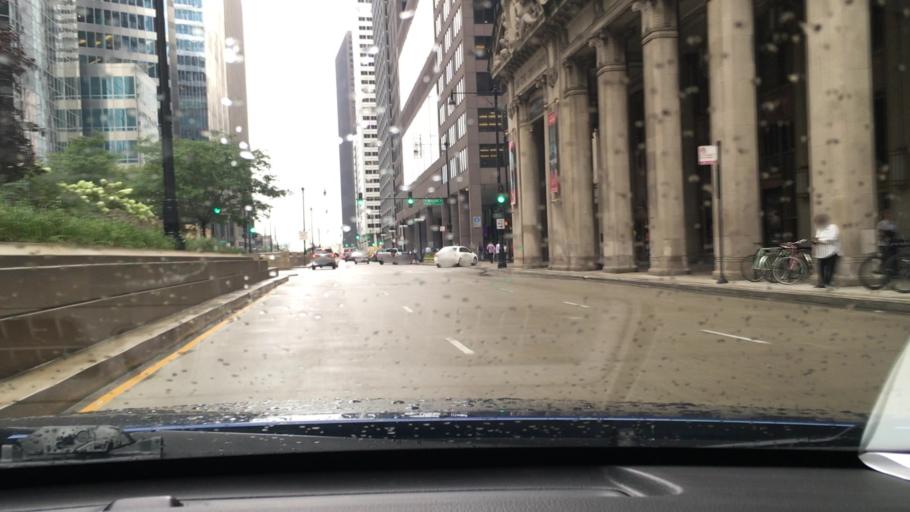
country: US
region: Illinois
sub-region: Cook County
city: Chicago
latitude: 41.8826
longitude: -87.6371
